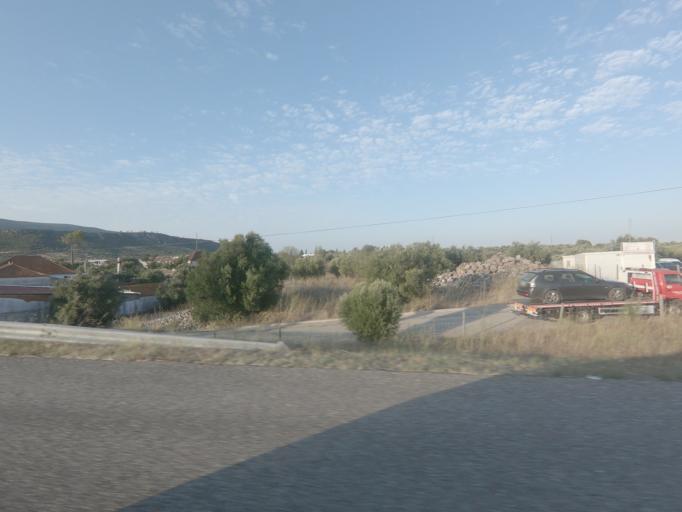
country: PT
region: Santarem
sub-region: Alcanena
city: Alcanena
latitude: 39.4799
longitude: -8.6338
